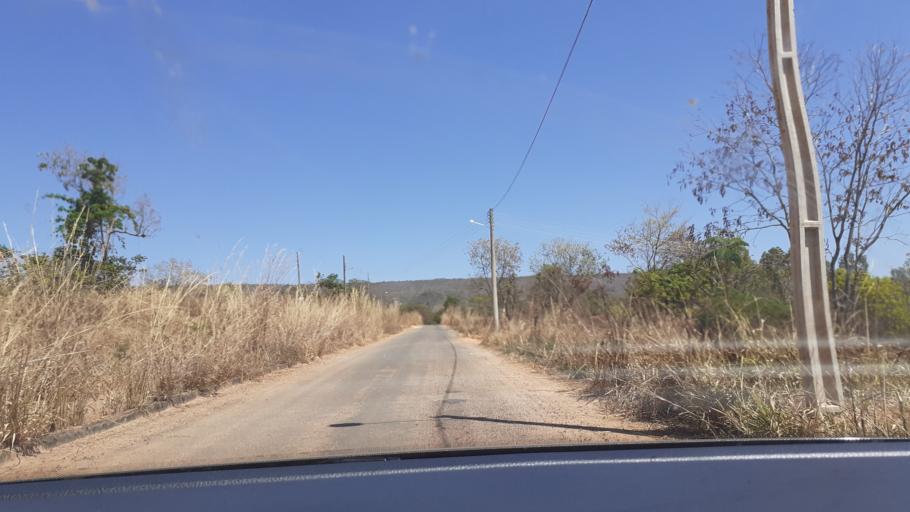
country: BR
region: Goias
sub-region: Caldas Novas
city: Caldas Novas
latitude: -17.7417
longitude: -48.6567
